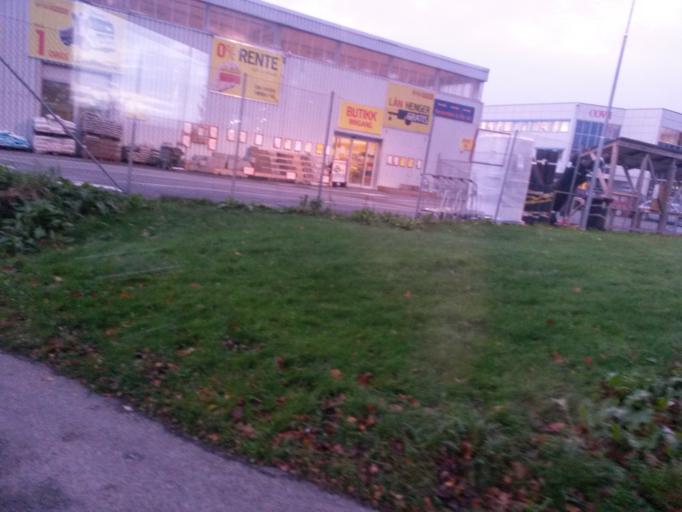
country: NO
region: Rogaland
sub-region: Stavanger
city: Stavanger
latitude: 58.9455
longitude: 5.7300
